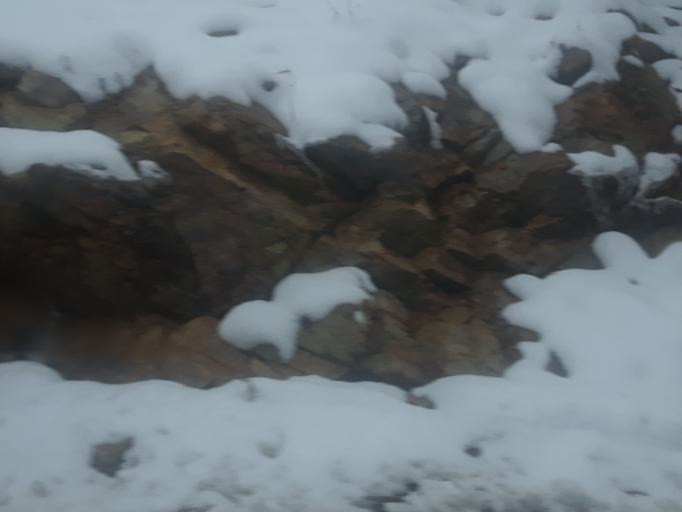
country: US
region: Colorado
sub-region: Boulder County
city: Coal Creek
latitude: 39.9203
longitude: -105.3736
